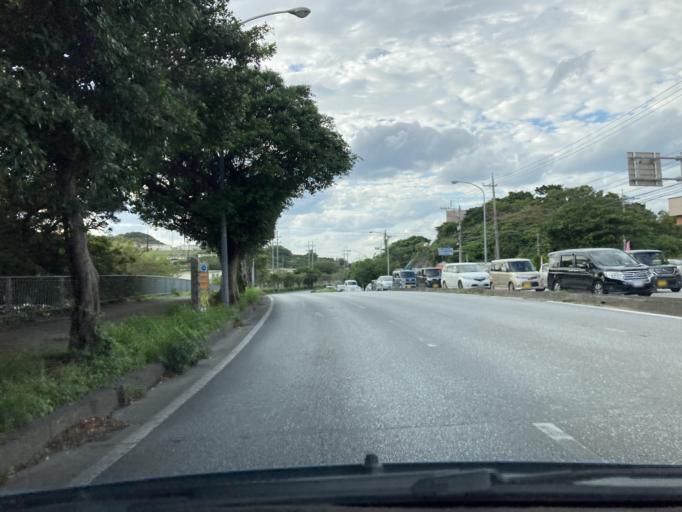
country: JP
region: Okinawa
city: Okinawa
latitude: 26.3564
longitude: 127.8039
